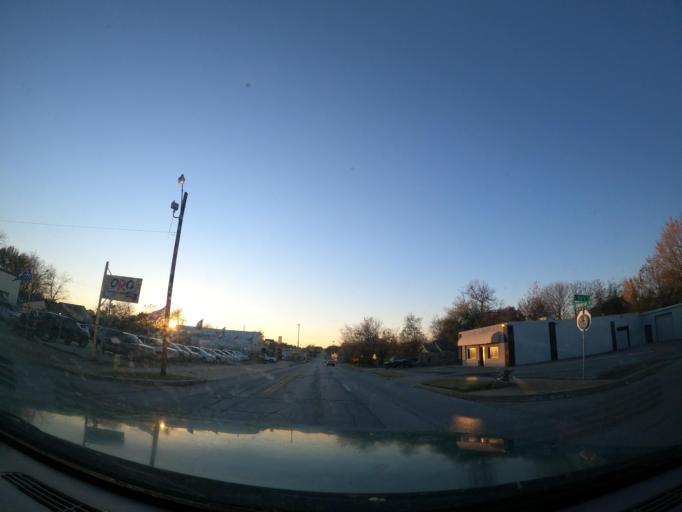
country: US
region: Oklahoma
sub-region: Tulsa County
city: Tulsa
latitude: 36.1608
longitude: -95.9426
